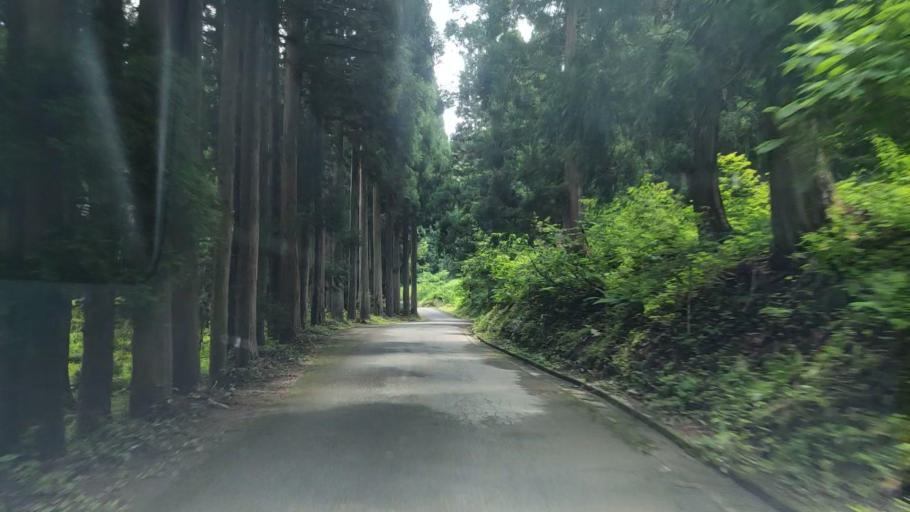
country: JP
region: Fukui
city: Ono
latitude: 35.8099
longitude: 136.4644
